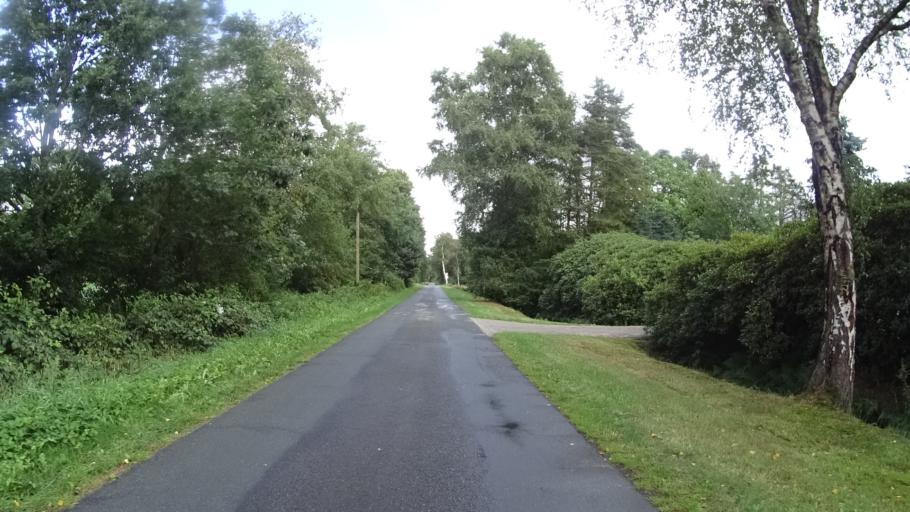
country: DE
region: Lower Saxony
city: Friedeburg
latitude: 53.3819
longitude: 7.8601
